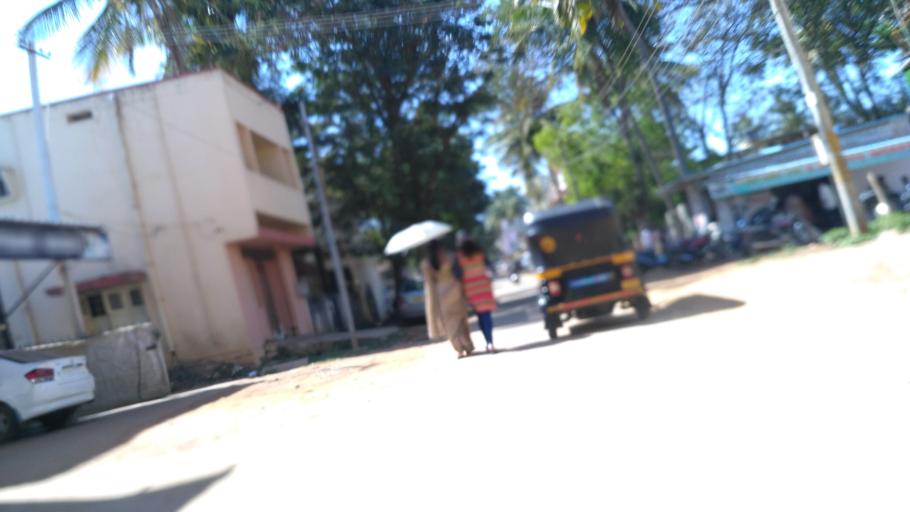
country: IN
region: Karnataka
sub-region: Hassan
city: Hassan
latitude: 13.0070
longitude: 76.1089
